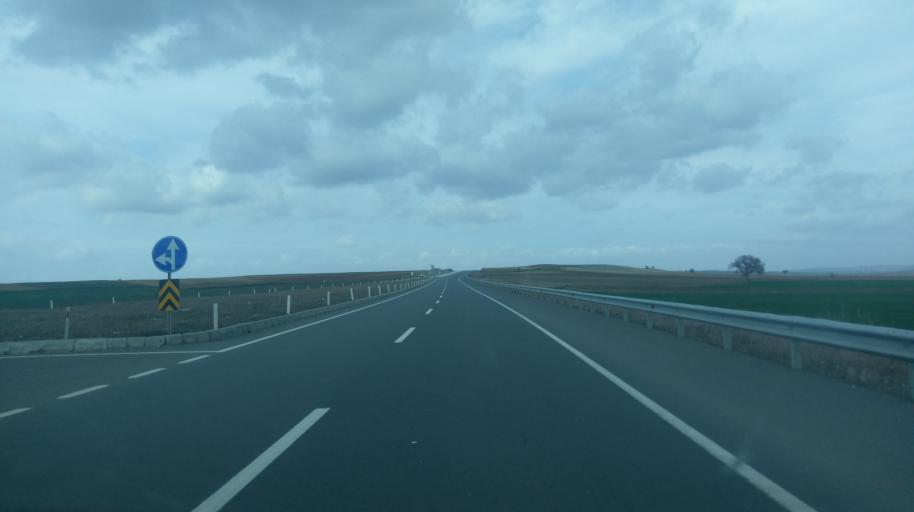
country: TR
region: Edirne
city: Ibriktepe
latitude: 41.0111
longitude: 26.6370
